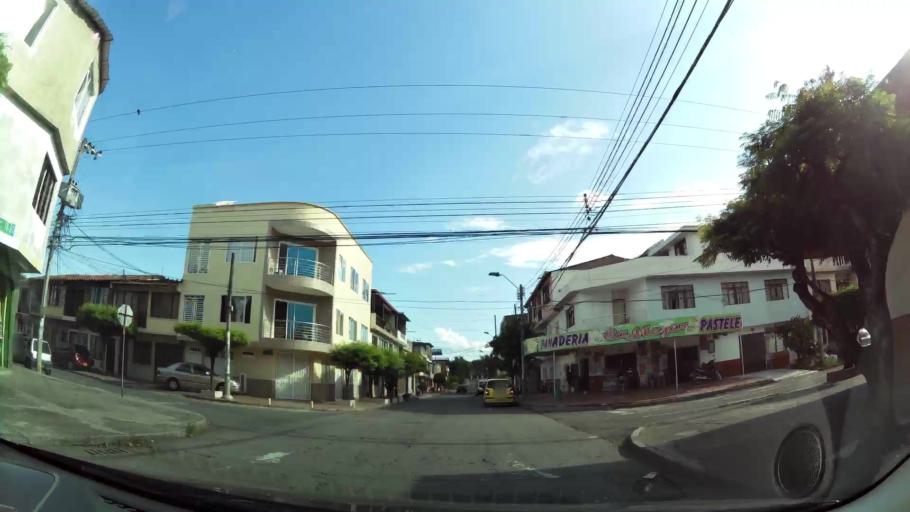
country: CO
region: Valle del Cauca
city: Cali
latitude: 3.4200
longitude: -76.5258
